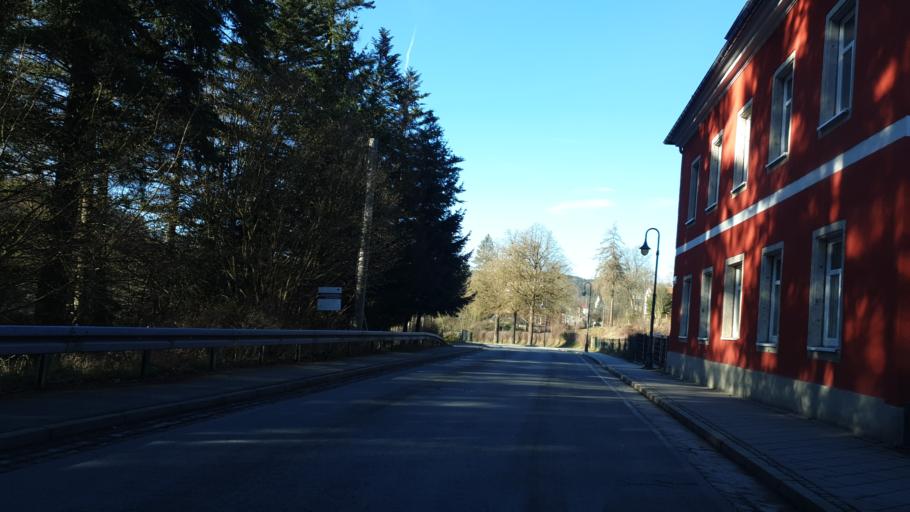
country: DE
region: Saxony
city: Bad Elster
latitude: 50.2776
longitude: 12.2423
